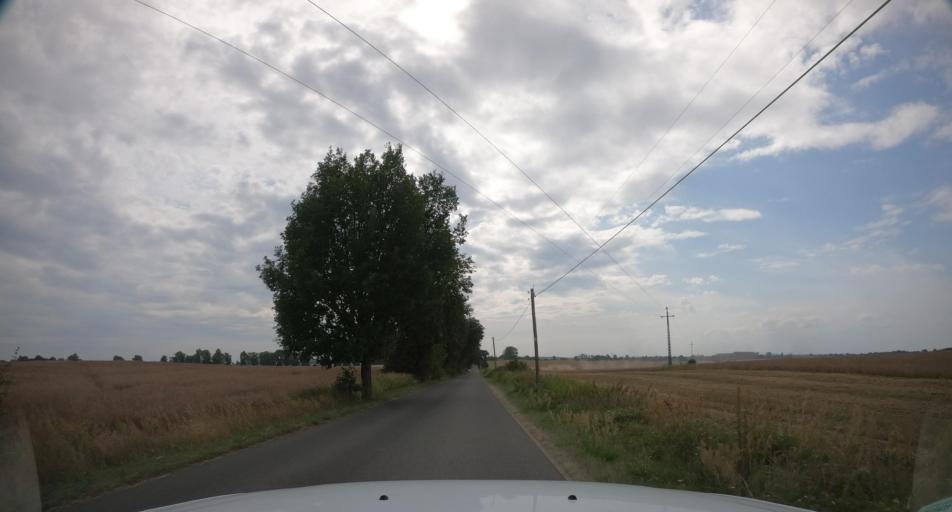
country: PL
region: West Pomeranian Voivodeship
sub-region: Powiat walecki
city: Tuczno
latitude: 53.2281
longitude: 16.2213
